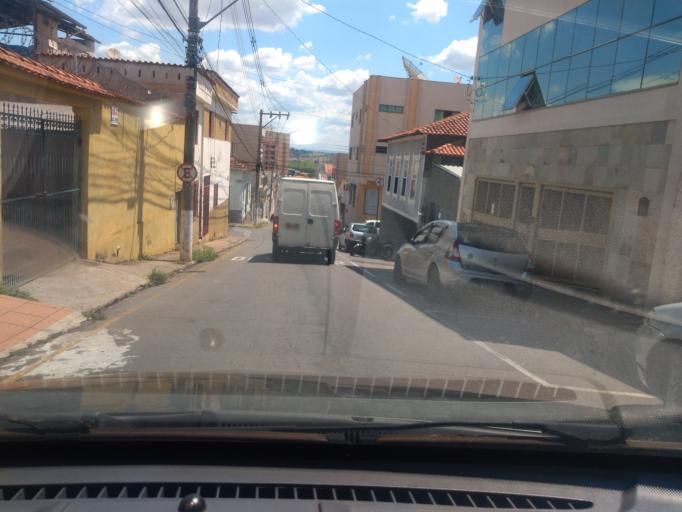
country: BR
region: Minas Gerais
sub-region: Tres Coracoes
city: Tres Coracoes
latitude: -21.6967
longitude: -45.2525
